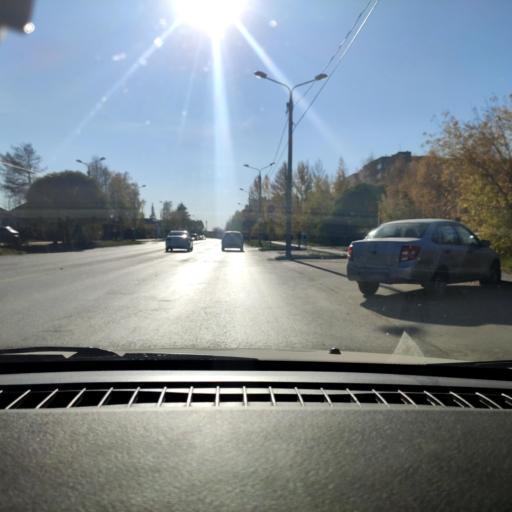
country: RU
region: Perm
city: Perm
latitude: 58.0574
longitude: 56.3577
